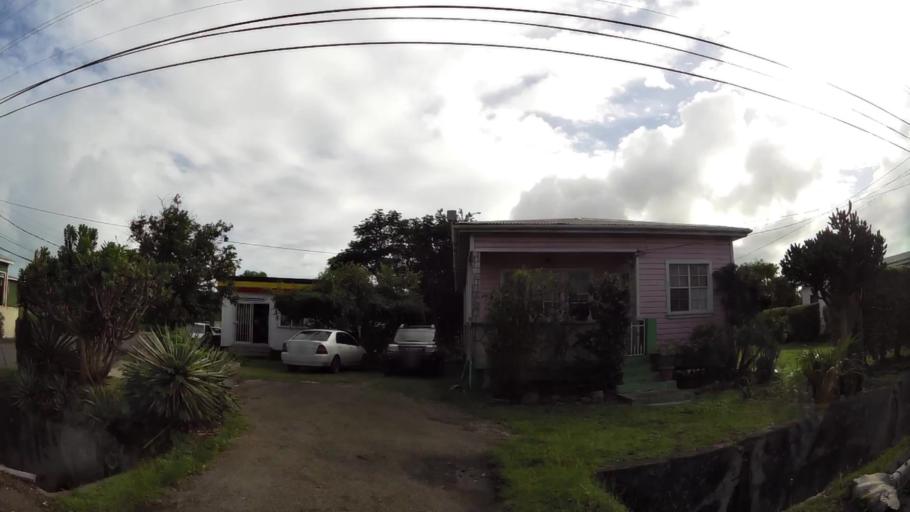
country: AG
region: Saint John
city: Saint John's
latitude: 17.1244
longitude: -61.8262
